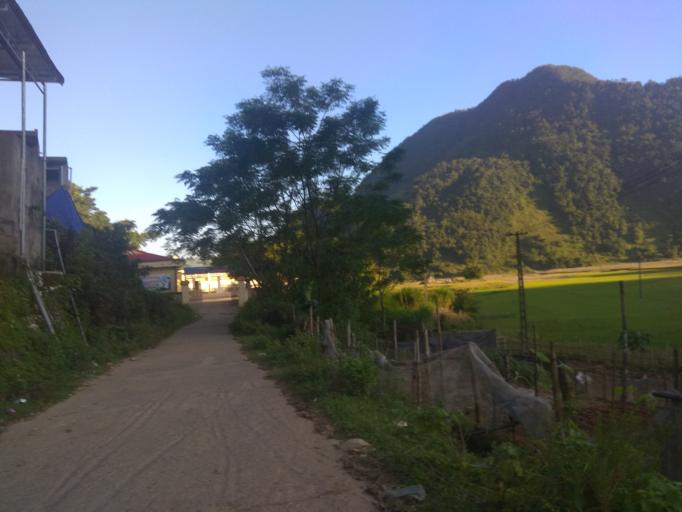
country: VN
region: Hoa Binh
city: Thi Tran Muong Khen
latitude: 20.5612
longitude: 105.1800
